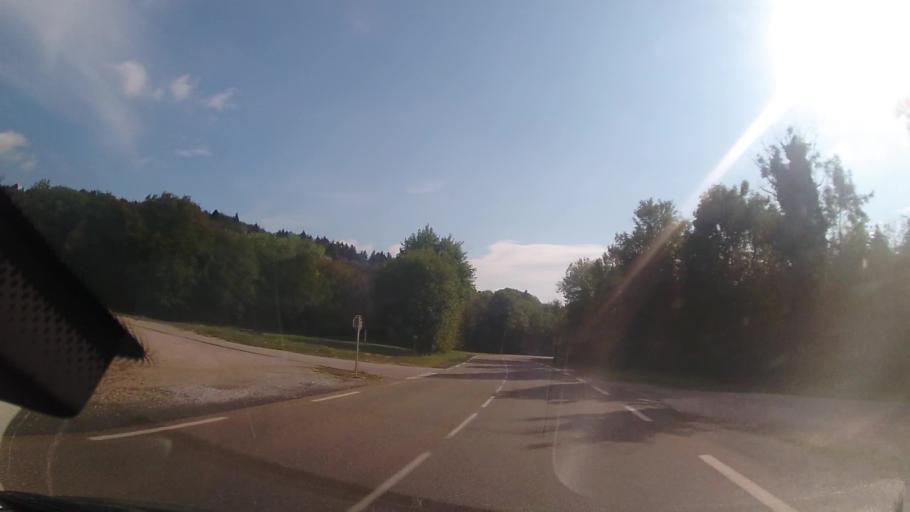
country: FR
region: Franche-Comte
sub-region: Departement du Jura
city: Clairvaux-les-Lacs
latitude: 46.5986
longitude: 5.8481
